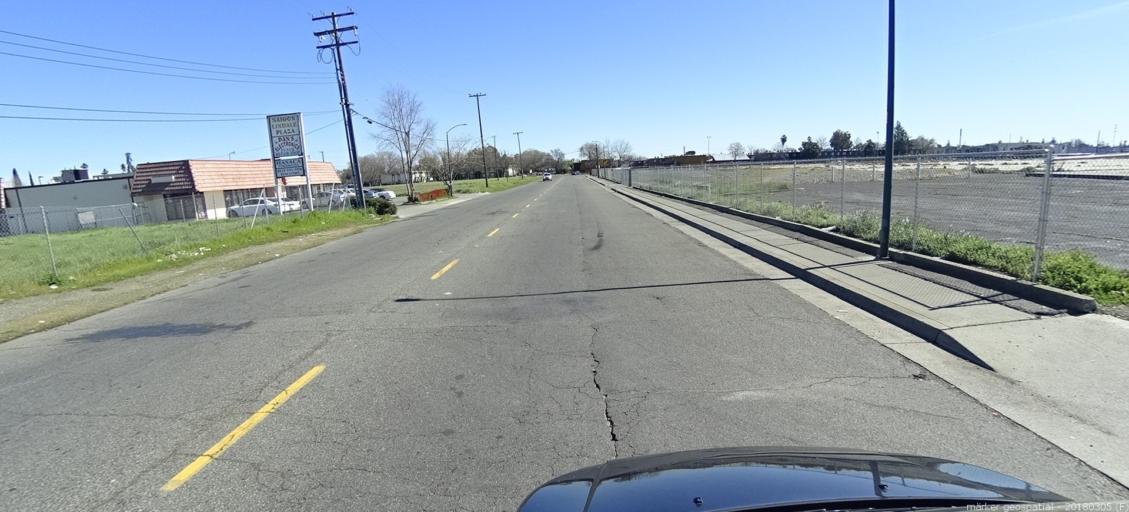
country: US
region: California
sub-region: Sacramento County
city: Florin
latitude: 38.4988
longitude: -121.4294
